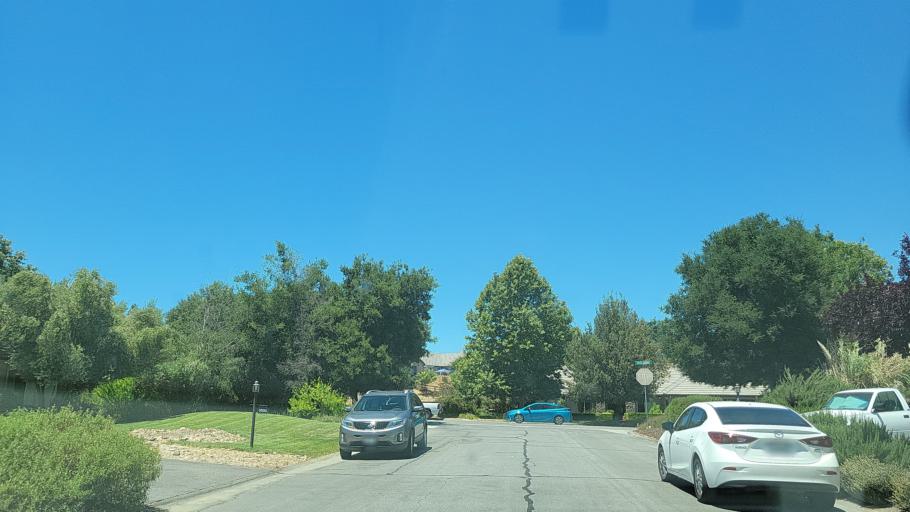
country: US
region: California
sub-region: San Luis Obispo County
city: Atascadero
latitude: 35.5152
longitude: -120.6768
